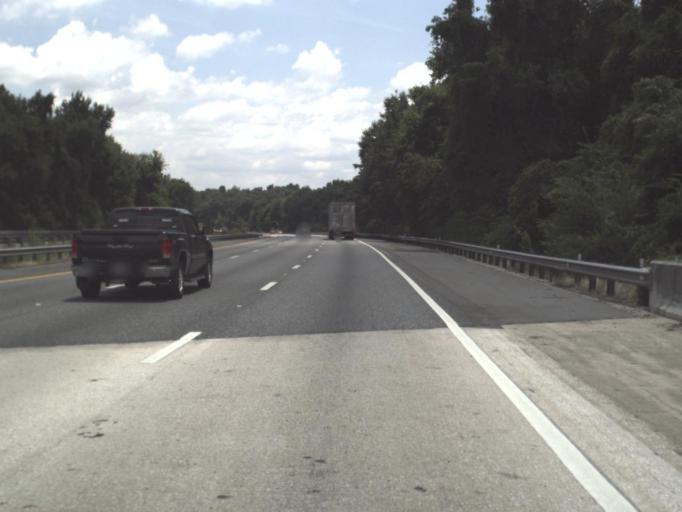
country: US
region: Florida
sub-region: Hamilton County
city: Jasper
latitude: 30.4988
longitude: -83.0409
